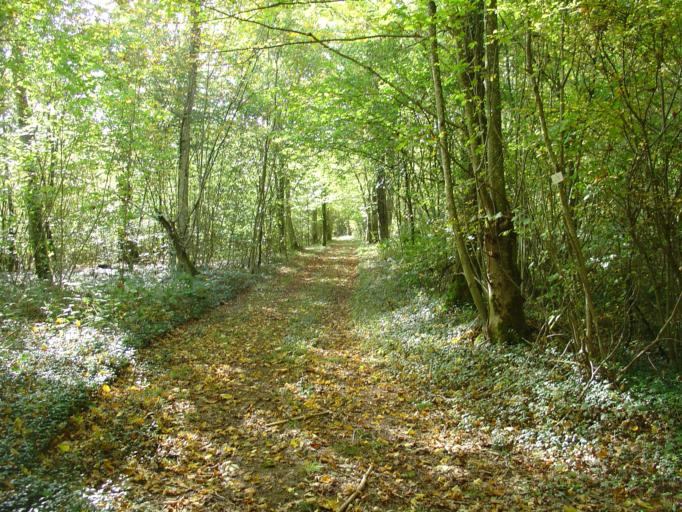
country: FR
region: Lorraine
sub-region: Departement de Meurthe-et-Moselle
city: Colombey-les-Belles
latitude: 48.5481
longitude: 5.9524
